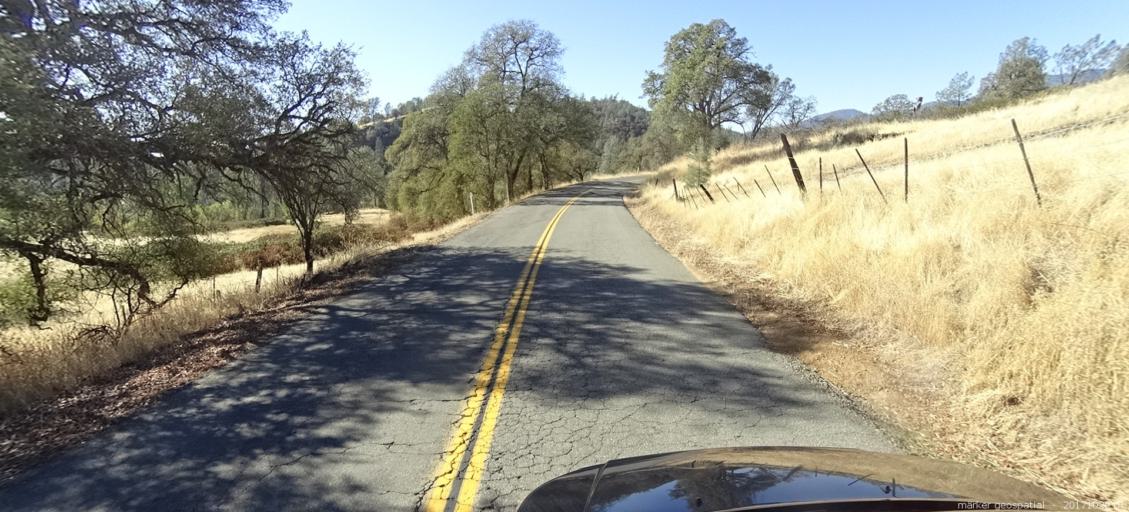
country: US
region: California
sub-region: Shasta County
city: Shasta
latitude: 40.4739
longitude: -122.6214
